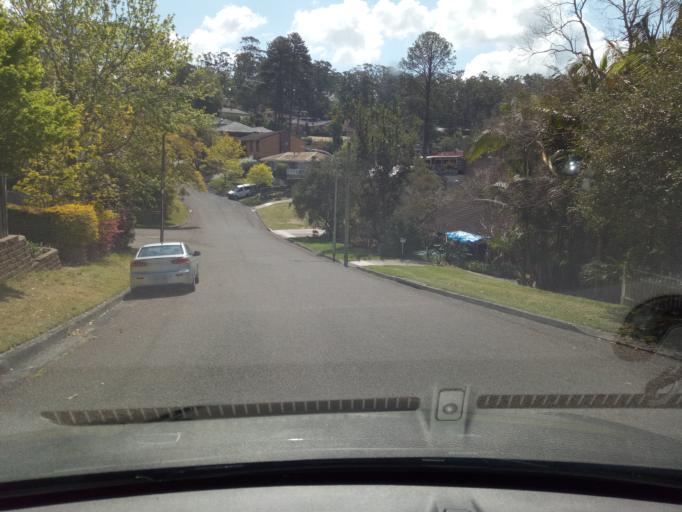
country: AU
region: New South Wales
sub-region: Gosford Shire
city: Narara
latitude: -33.3979
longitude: 151.3537
